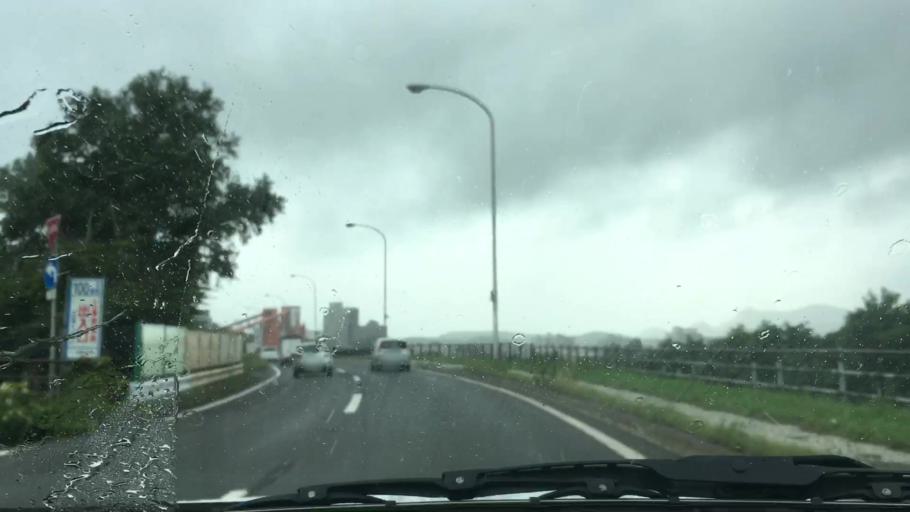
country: JP
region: Hokkaido
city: Sapporo
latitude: 43.0156
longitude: 141.3545
